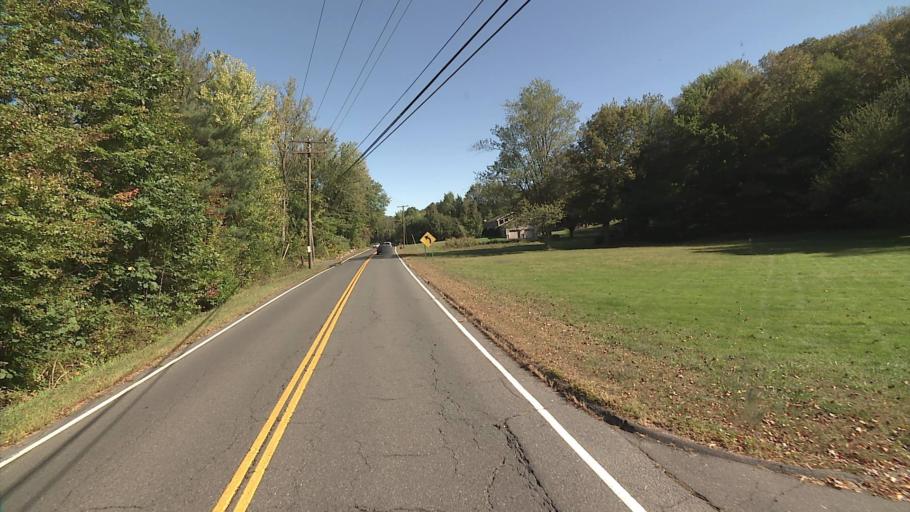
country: US
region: Connecticut
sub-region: Tolland County
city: Somers
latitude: 41.9539
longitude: -72.4468
